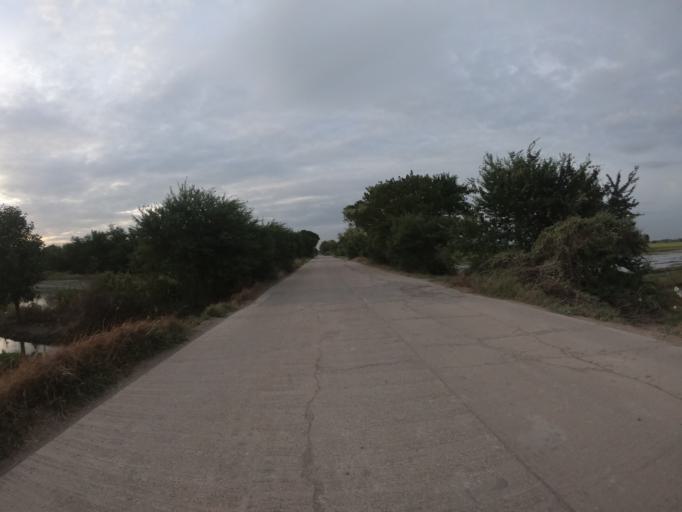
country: TH
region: Pathum Thani
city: Ban Lam Luk Ka
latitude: 14.0004
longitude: 100.8001
